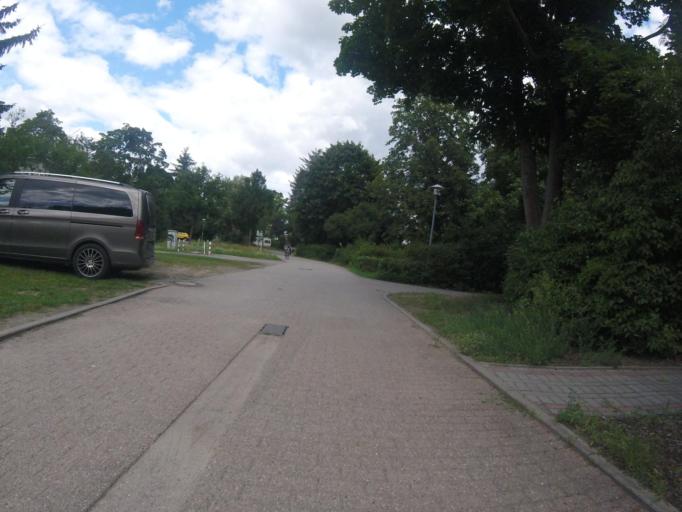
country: DE
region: Brandenburg
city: Konigs Wusterhausen
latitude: 52.2949
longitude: 13.6144
